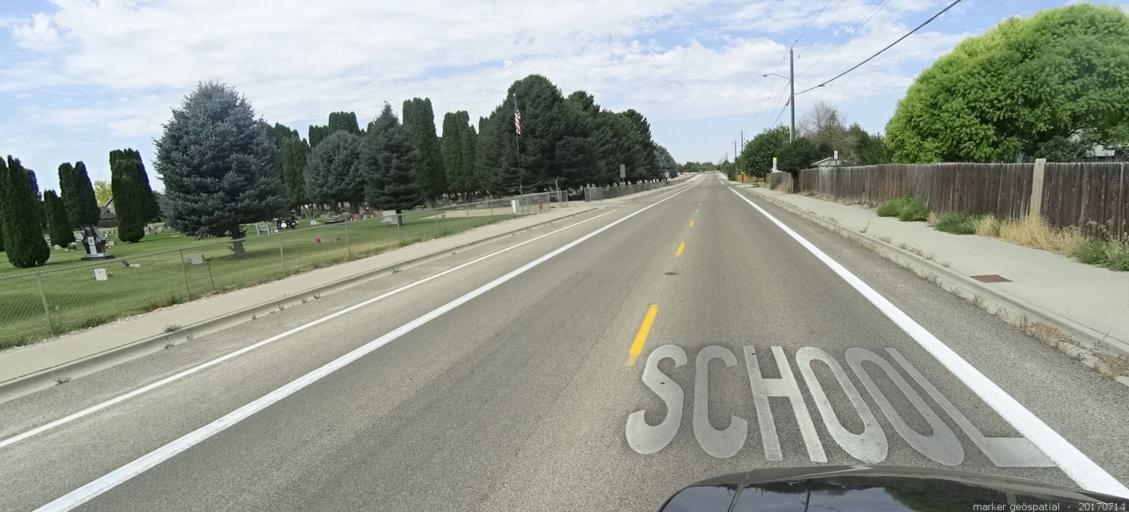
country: US
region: Idaho
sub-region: Ada County
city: Kuna
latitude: 43.4957
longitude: -116.4256
